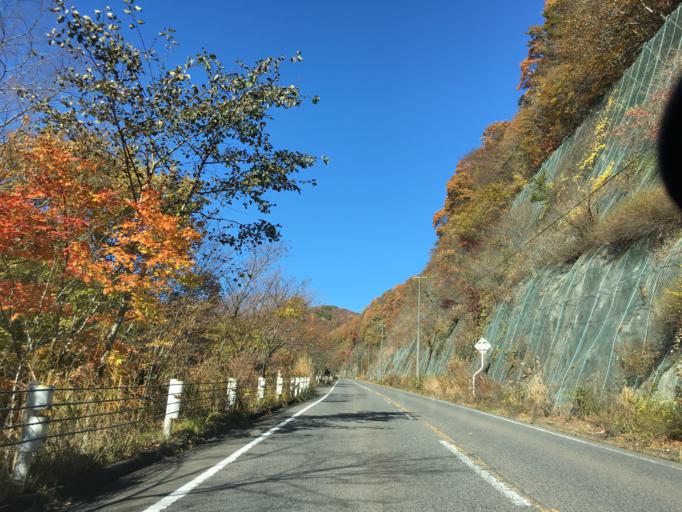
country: JP
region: Fukushima
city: Inawashiro
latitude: 37.3223
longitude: 140.1322
